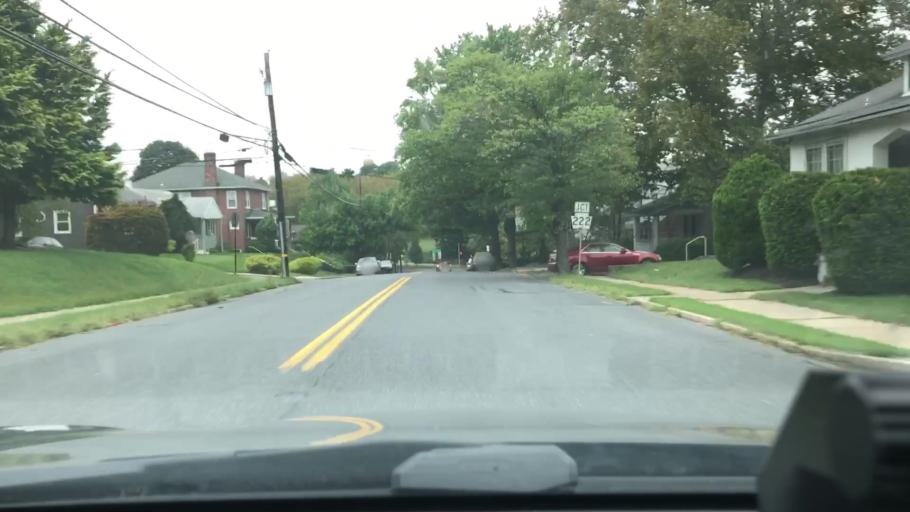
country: US
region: Pennsylvania
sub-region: Lehigh County
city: Dorneyville
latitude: 40.5912
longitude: -75.5063
